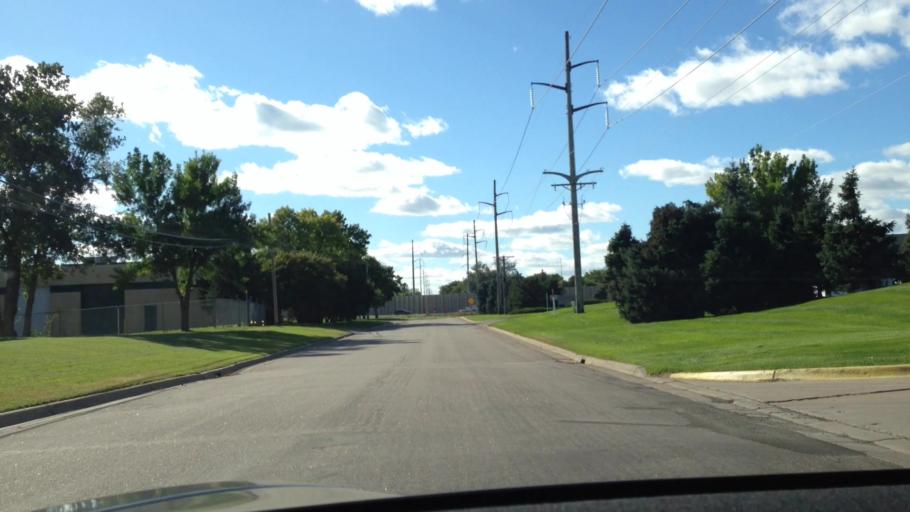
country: US
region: Minnesota
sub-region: Hennepin County
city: Osseo
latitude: 45.1161
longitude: -93.3872
